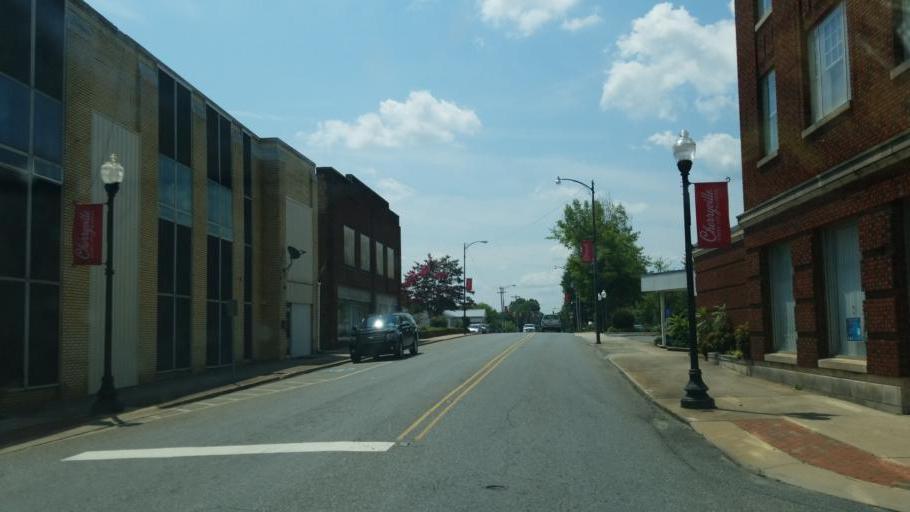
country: US
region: North Carolina
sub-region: Gaston County
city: Cherryville
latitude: 35.3790
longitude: -81.3796
